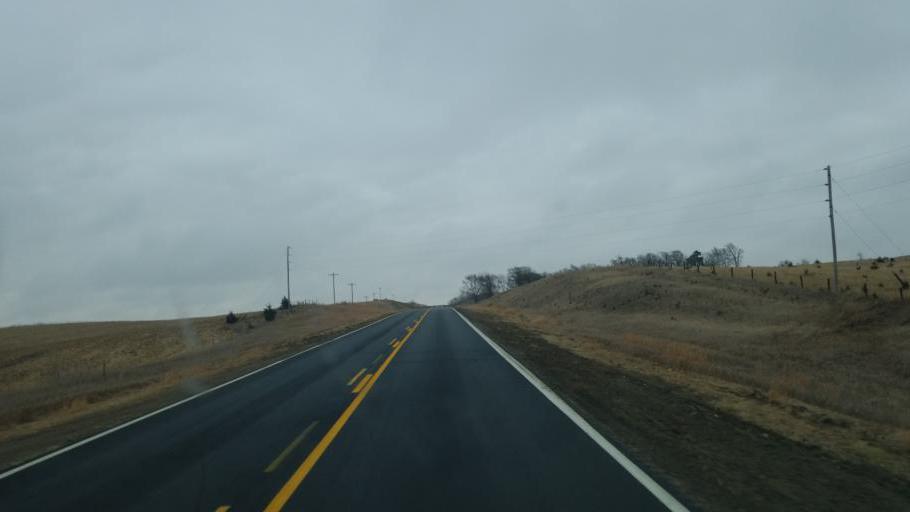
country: US
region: Nebraska
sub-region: Knox County
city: Bloomfield
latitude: 42.5973
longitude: -97.7502
